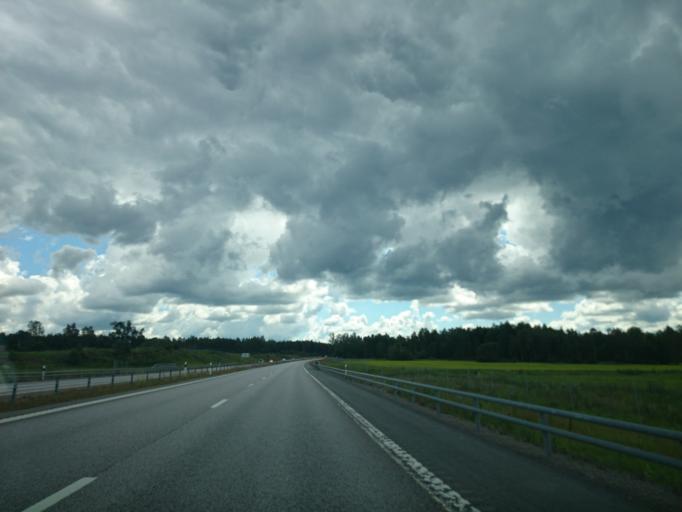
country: SE
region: Uppsala
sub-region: Tierps Kommun
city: Tierp
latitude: 60.3220
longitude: 17.5142
